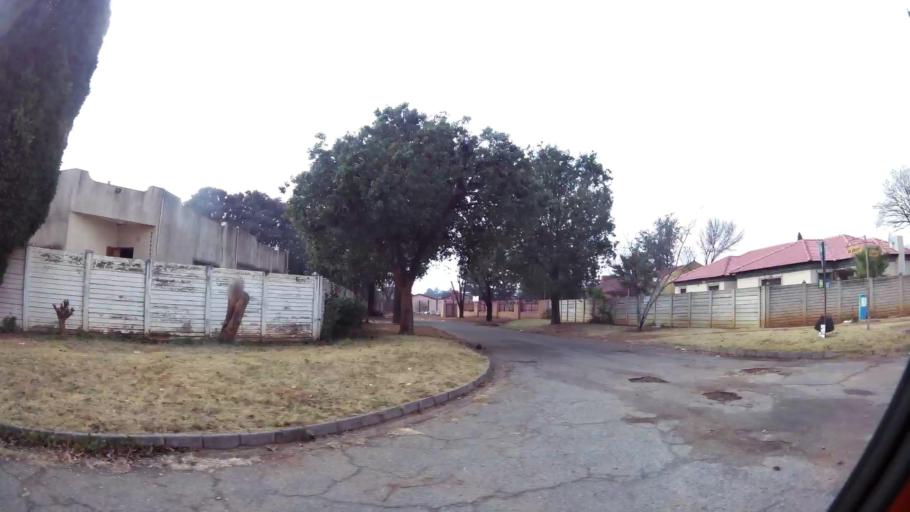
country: ZA
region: Gauteng
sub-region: Sedibeng District Municipality
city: Vanderbijlpark
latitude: -26.6952
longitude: 27.8511
